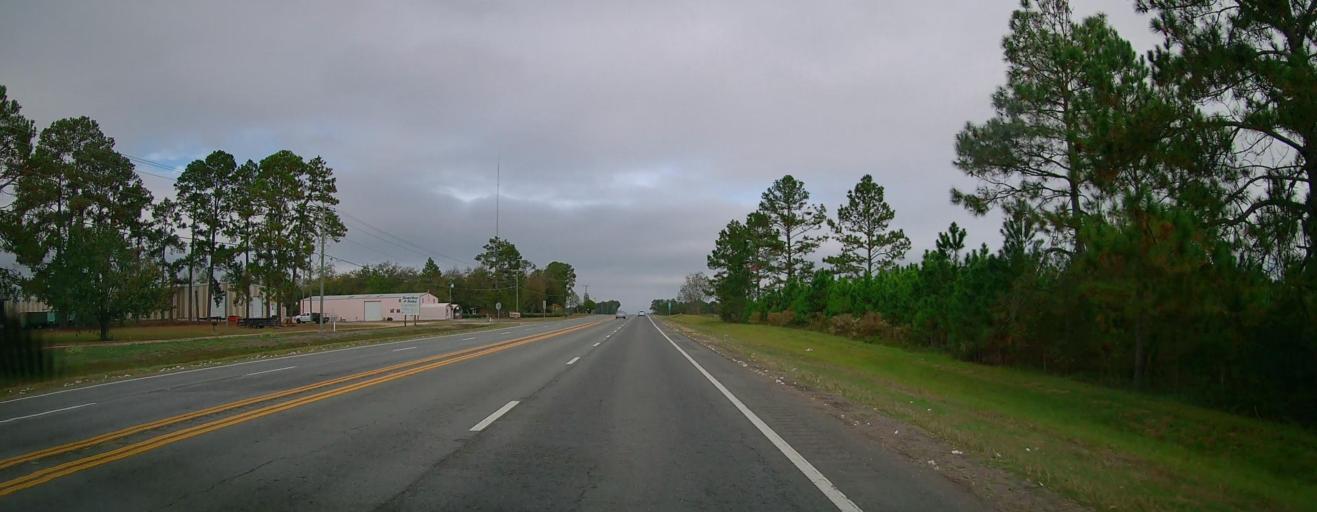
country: US
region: Georgia
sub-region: Tift County
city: Omega
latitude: 31.3574
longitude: -83.5807
